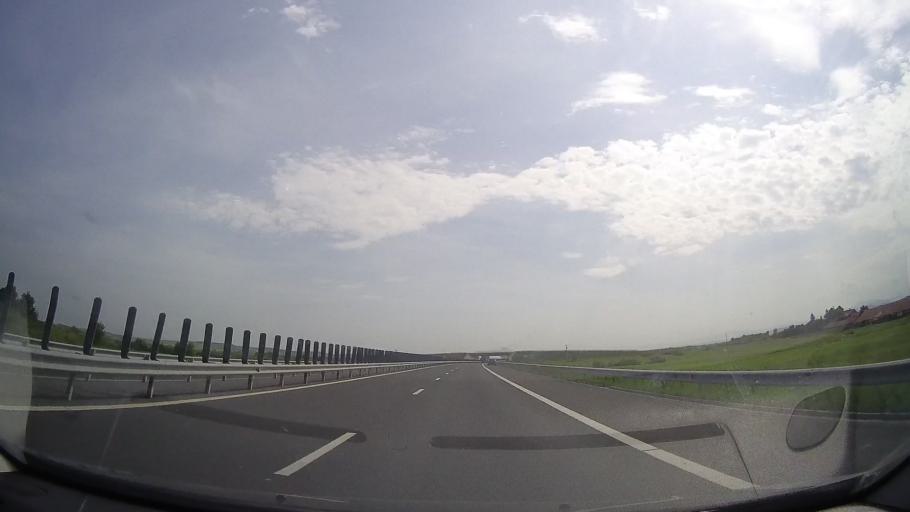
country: RO
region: Timis
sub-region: Comuna Bethausen
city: Bethausen
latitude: 45.8141
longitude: 21.9533
